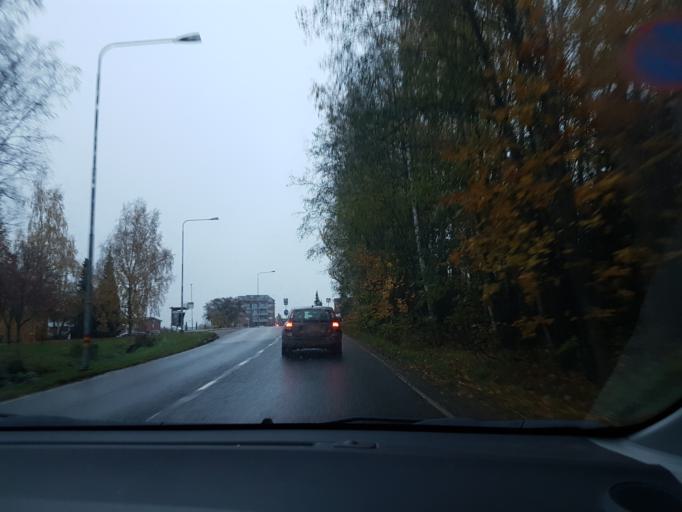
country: FI
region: Uusimaa
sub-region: Helsinki
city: Tuusula
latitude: 60.4036
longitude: 25.0222
